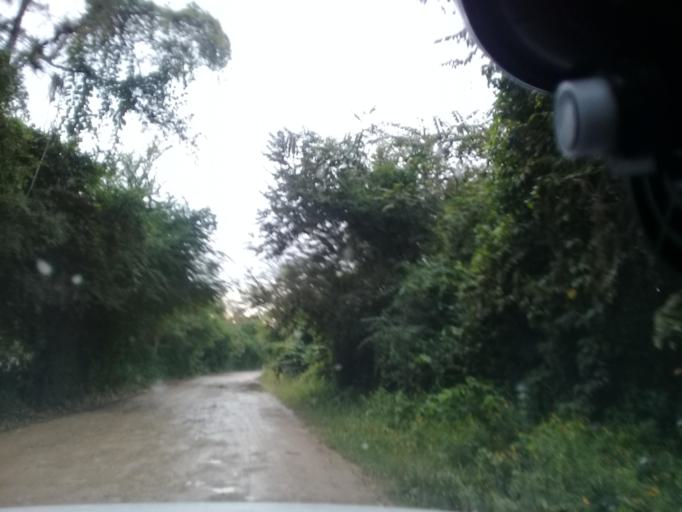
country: MX
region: Hidalgo
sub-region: Huejutla de Reyes
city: Chalahuiyapa
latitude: 21.1574
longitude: -98.3715
